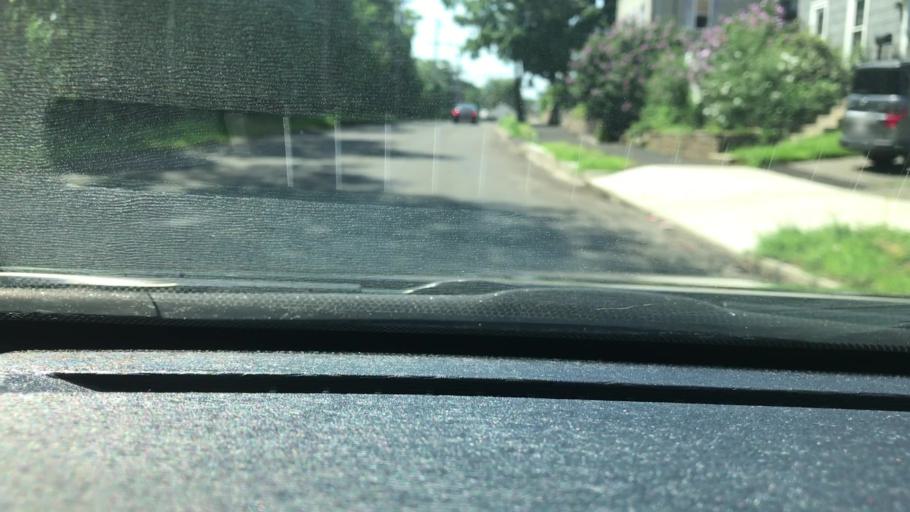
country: US
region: Massachusetts
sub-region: Middlesex County
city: Wakefield
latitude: 42.5043
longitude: -71.0662
